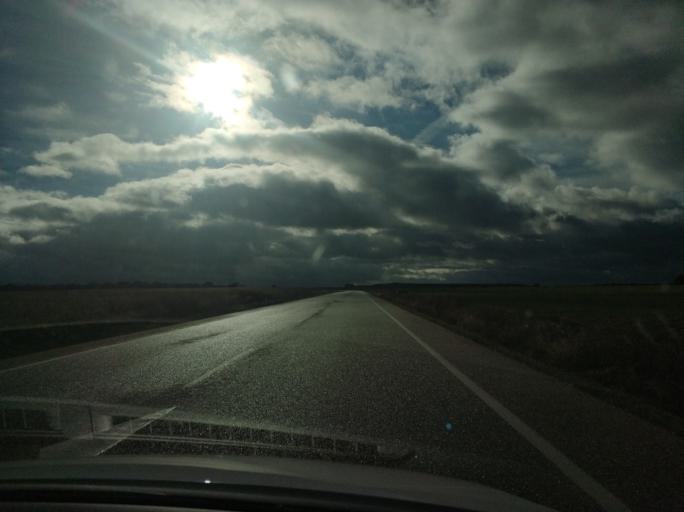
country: ES
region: Castille and Leon
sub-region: Provincia de Segovia
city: Corral de Ayllon
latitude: 41.3994
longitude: -3.4253
